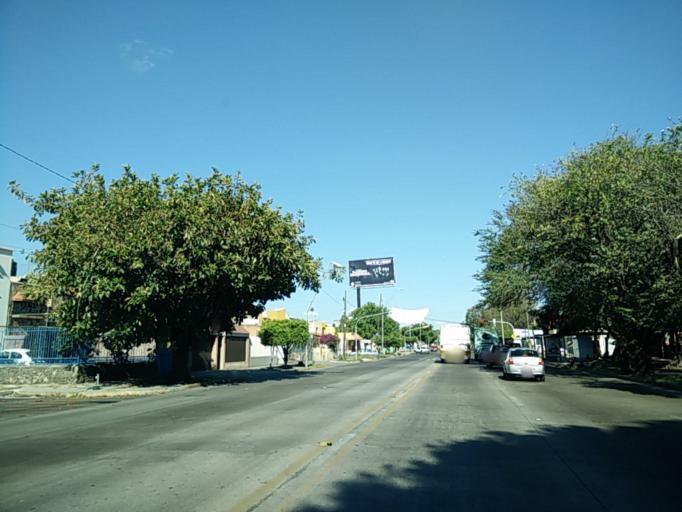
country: MX
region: Jalisco
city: Tlaquepaque
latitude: 20.6593
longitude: -103.3303
